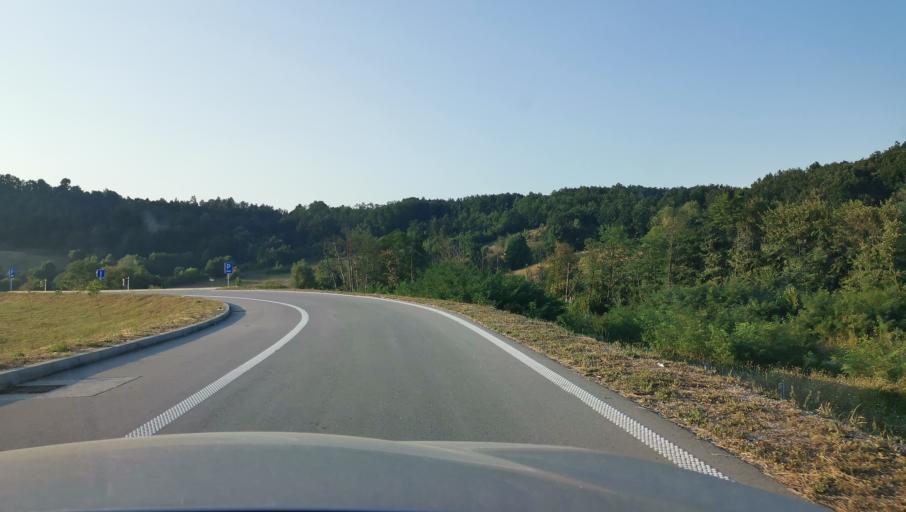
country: RS
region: Central Serbia
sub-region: Kolubarski Okrug
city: Ljig
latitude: 44.1675
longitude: 20.3140
